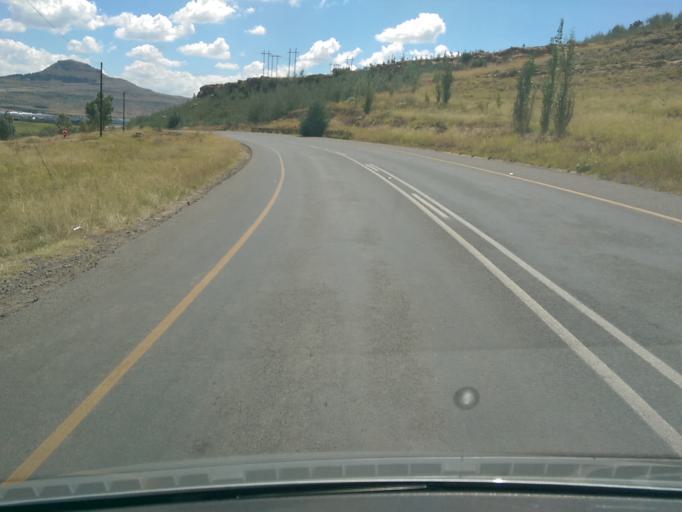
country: LS
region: Maseru
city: Maseru
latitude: -29.3802
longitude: 27.5020
